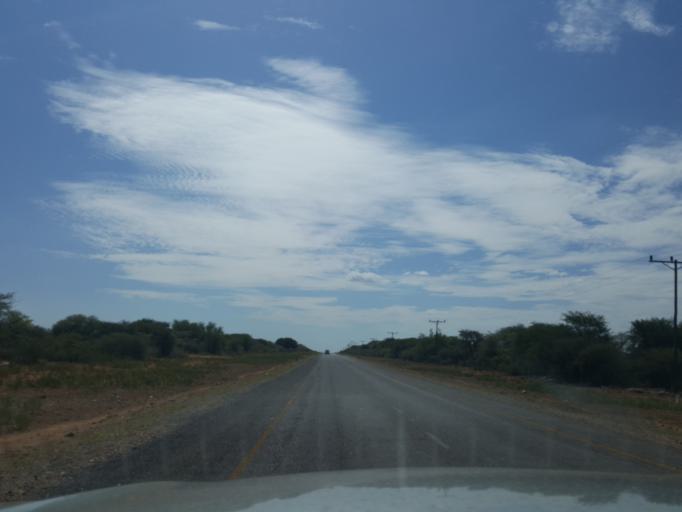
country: BW
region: Kweneng
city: Letlhakeng
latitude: -24.1488
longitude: 25.1538
